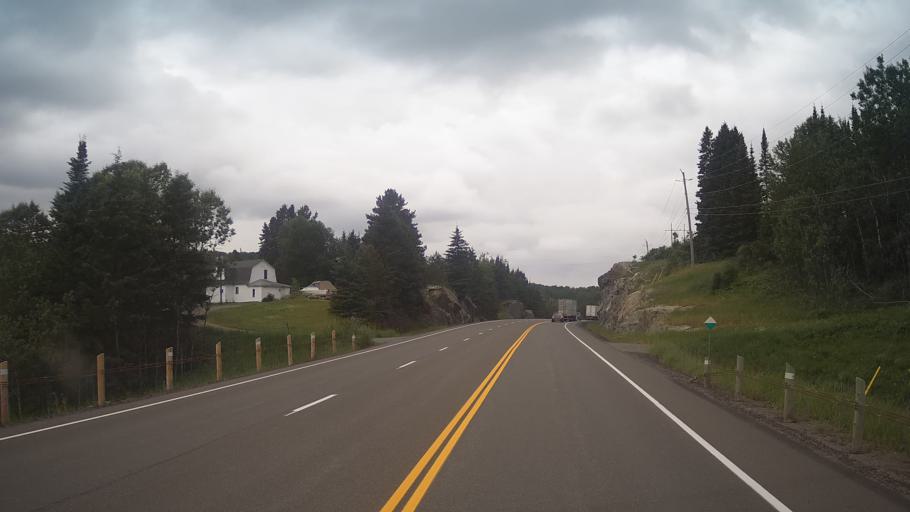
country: CA
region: Ontario
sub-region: Thunder Bay District
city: Thunder Bay
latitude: 48.5200
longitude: -89.5091
